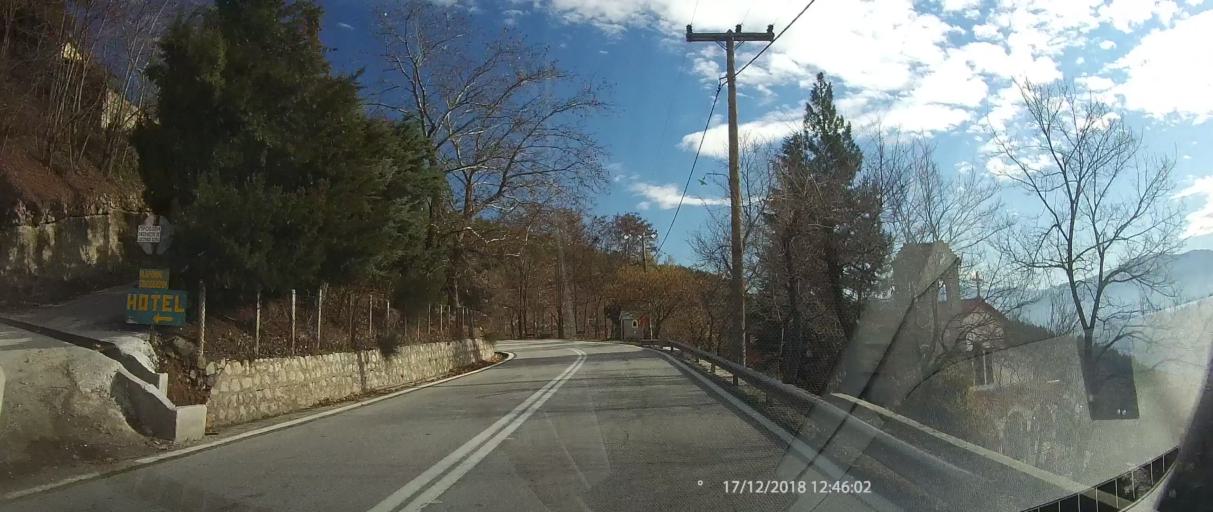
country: GR
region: Thessaly
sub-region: Trikala
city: Kastraki
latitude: 39.7880
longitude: 21.4141
